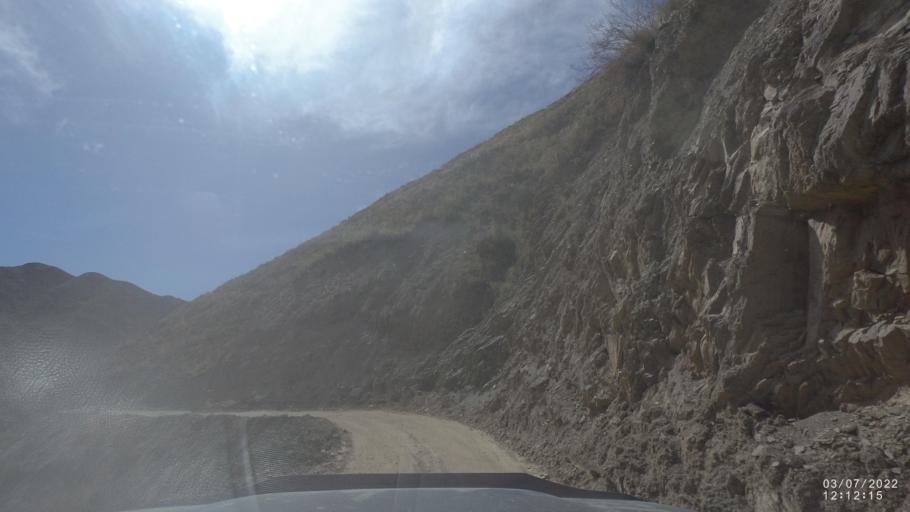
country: BO
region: Cochabamba
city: Irpa Irpa
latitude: -17.8391
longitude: -66.6131
